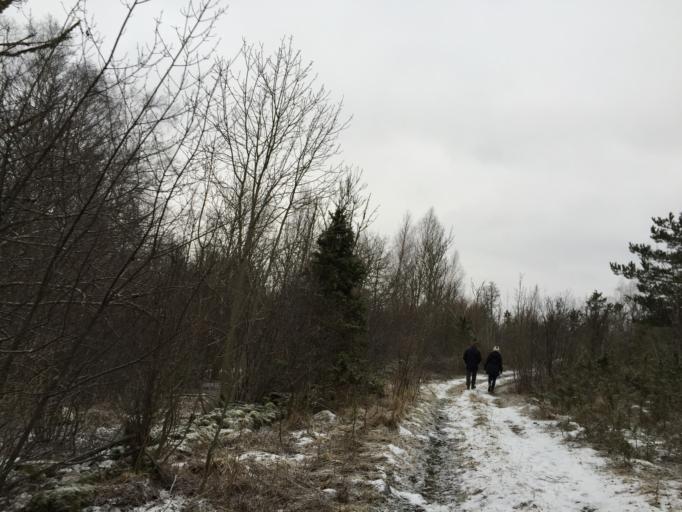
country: EE
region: Saare
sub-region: Orissaare vald
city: Orissaare
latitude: 58.6688
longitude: 23.2422
